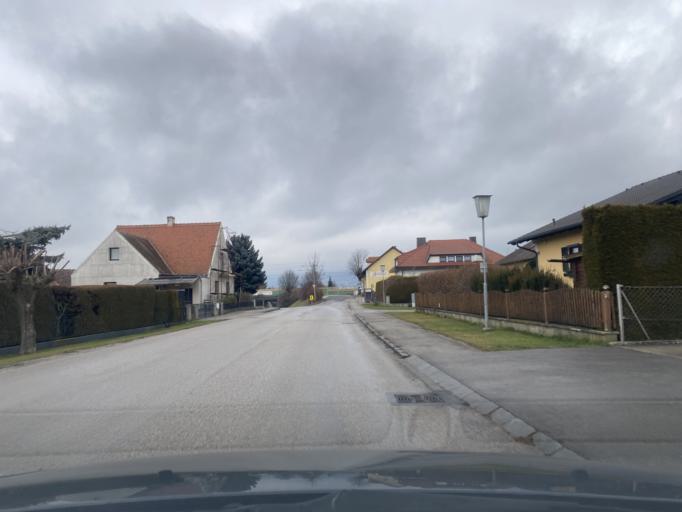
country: AT
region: Lower Austria
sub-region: Politischer Bezirk Sankt Polten
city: Prinzersdorf
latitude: 48.1954
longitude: 15.4985
